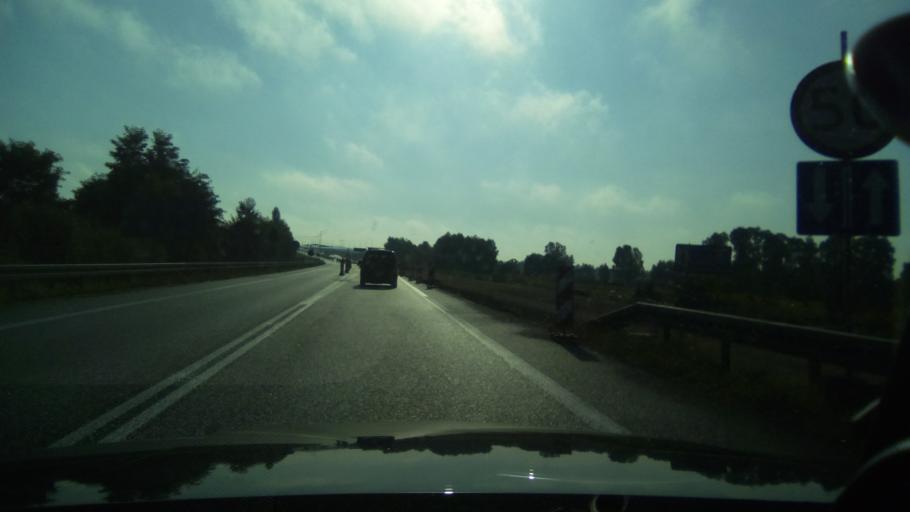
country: PL
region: Silesian Voivodeship
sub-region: Powiat bedzinski
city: Siewierz
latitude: 50.4209
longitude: 19.1933
